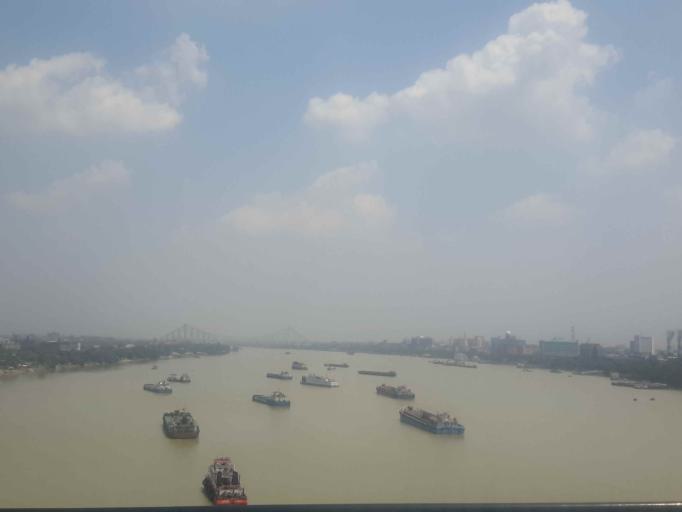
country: IN
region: West Bengal
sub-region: Haora
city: Haora
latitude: 22.5577
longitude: 88.3273
